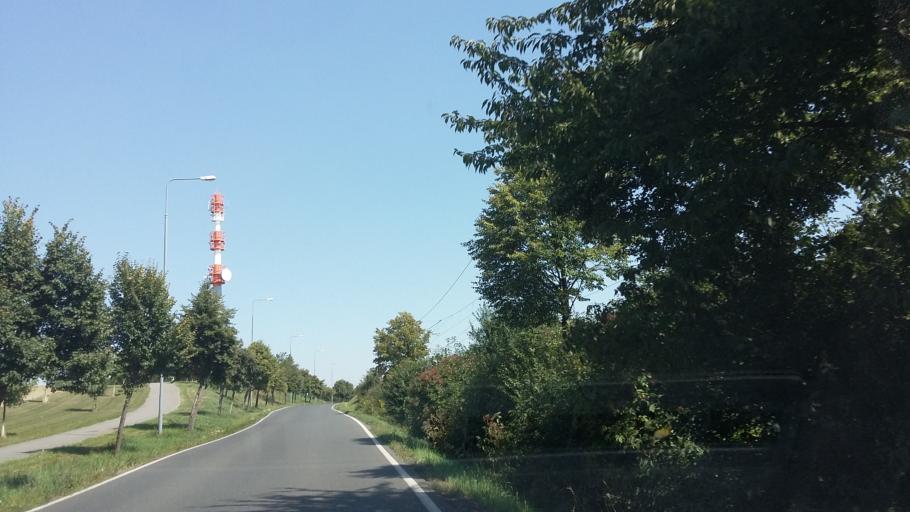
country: CZ
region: Central Bohemia
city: Zelenec
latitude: 50.1245
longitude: 14.6408
